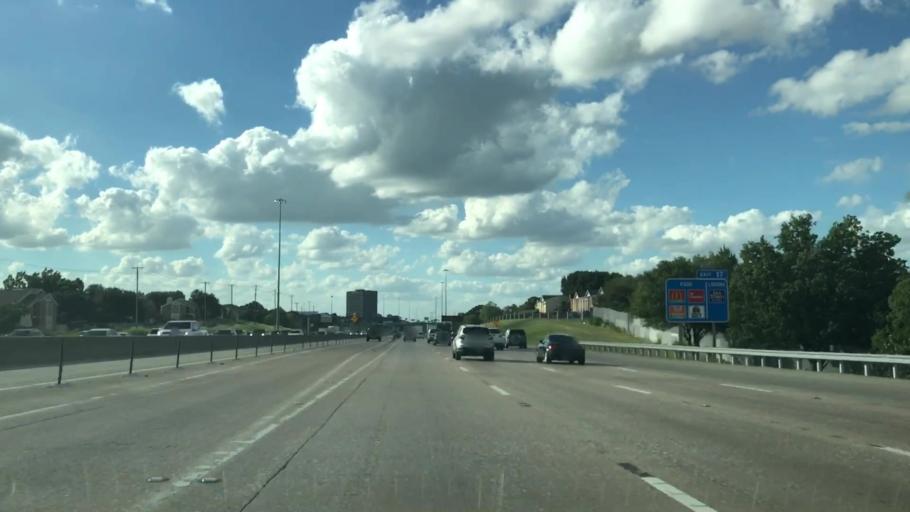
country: US
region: Texas
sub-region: Dallas County
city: Richardson
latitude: 32.9033
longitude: -96.7221
